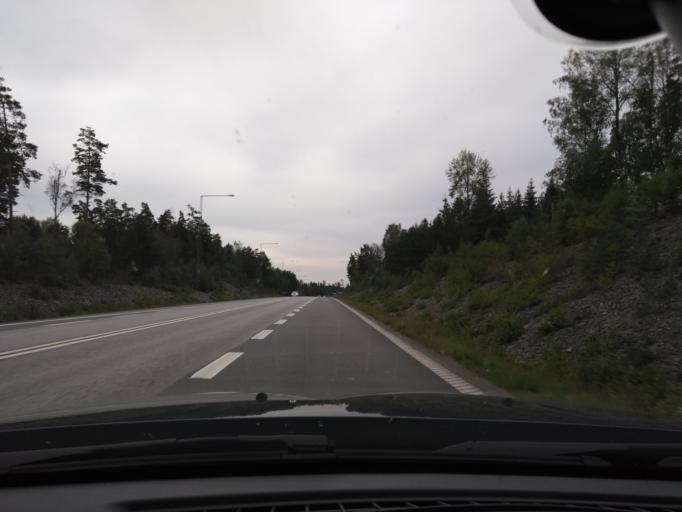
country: SE
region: Joenkoeping
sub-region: Eksjo Kommun
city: Eksjoe
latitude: 57.6548
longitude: 14.9545
